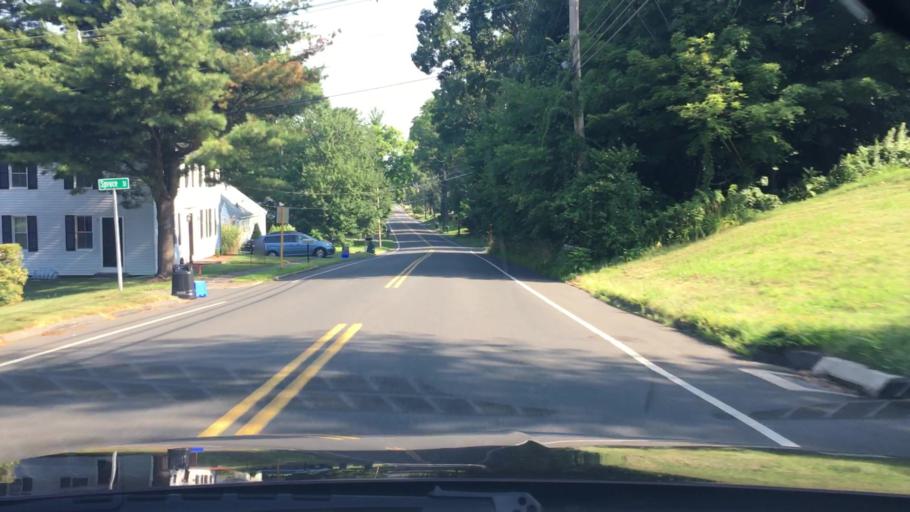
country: US
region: Massachusetts
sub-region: Hampden County
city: East Longmeadow
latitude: 42.0584
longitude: -72.5118
